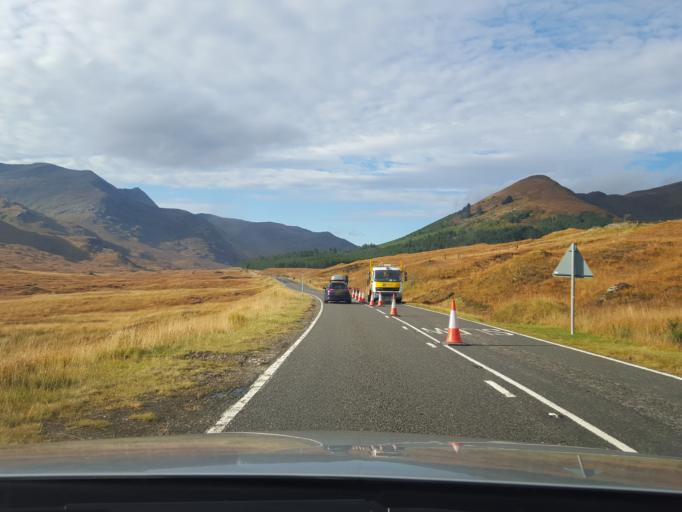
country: GB
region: Scotland
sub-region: Highland
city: Fort William
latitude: 57.1530
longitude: -5.1999
